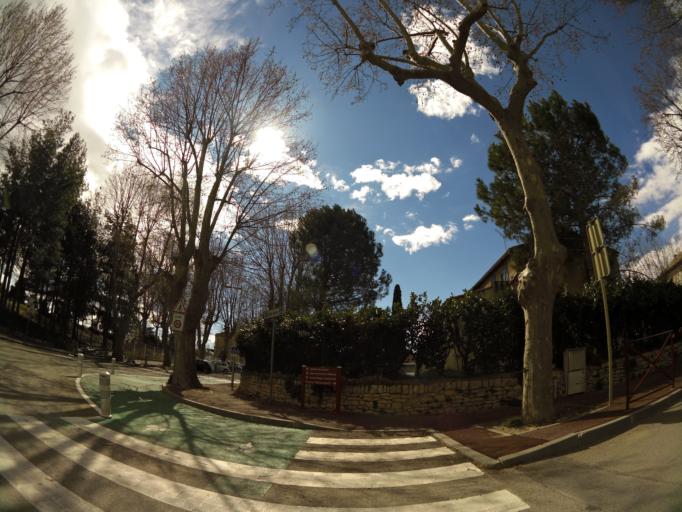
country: FR
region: Languedoc-Roussillon
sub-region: Departement du Gard
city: Calvisson
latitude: 43.7803
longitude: 4.1940
